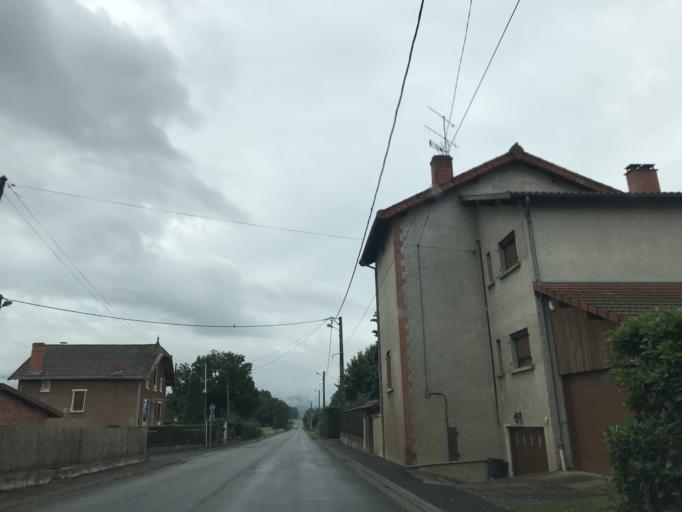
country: FR
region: Auvergne
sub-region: Departement du Puy-de-Dome
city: Arlanc
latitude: 45.4056
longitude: 3.7293
